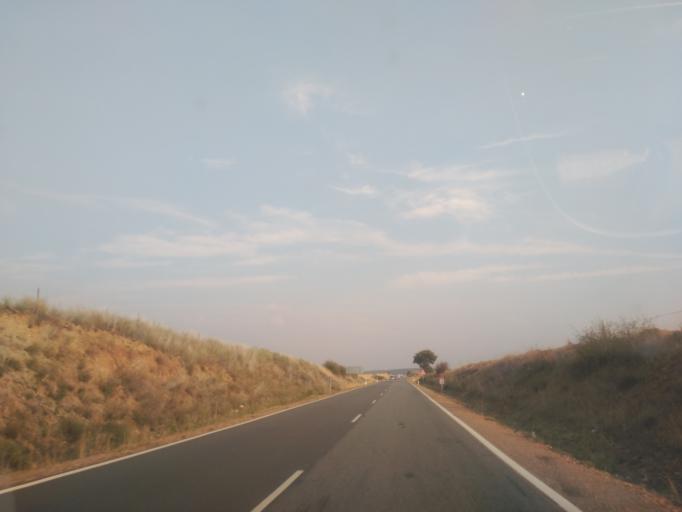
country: ES
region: Castille and Leon
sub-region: Provincia de Zamora
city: Pozuelo de Tabara
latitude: 41.7786
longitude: -5.8860
